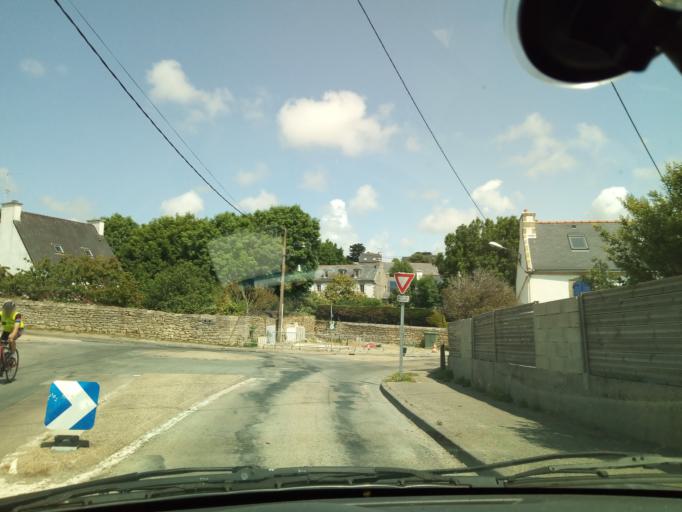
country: FR
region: Brittany
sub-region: Departement du Finistere
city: Esquibien
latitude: 48.0094
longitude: -4.5568
